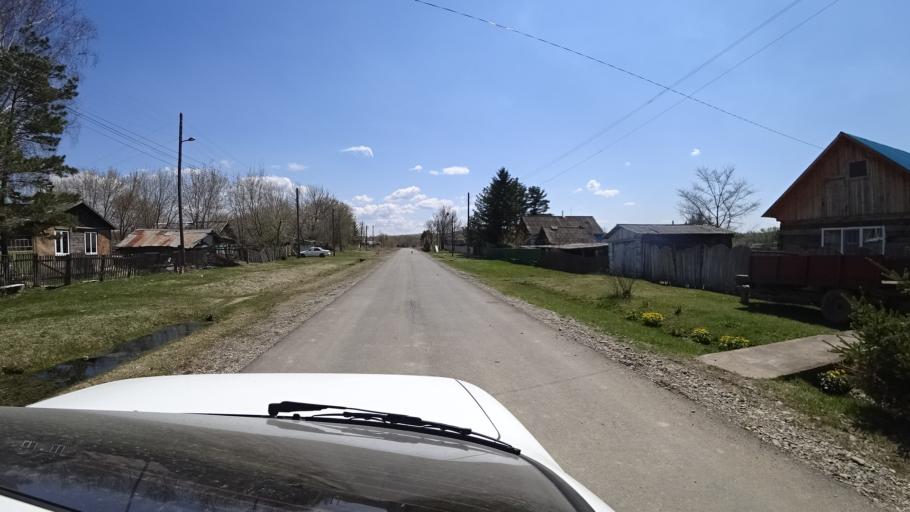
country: RU
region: Primorskiy
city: Dal'nerechensk
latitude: 45.7932
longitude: 133.7693
